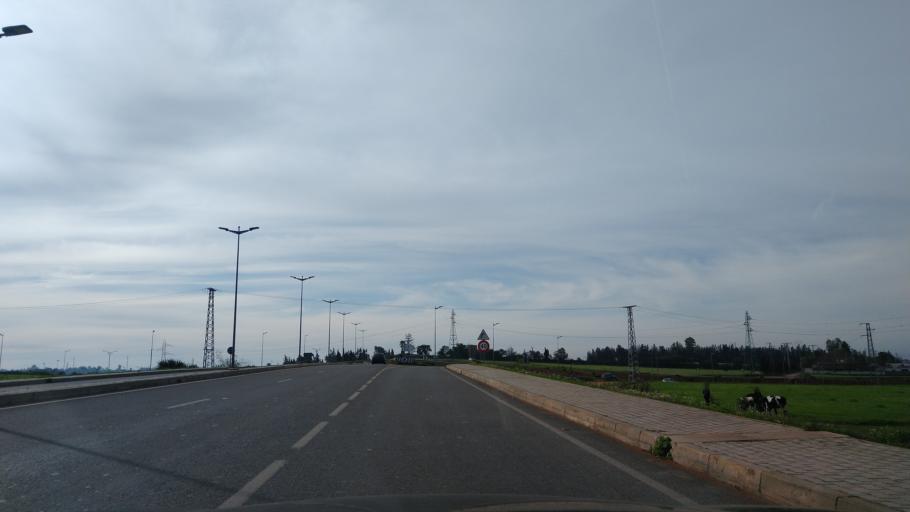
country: MA
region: Rabat-Sale-Zemmour-Zaer
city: Sale
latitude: 33.9831
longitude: -6.7401
